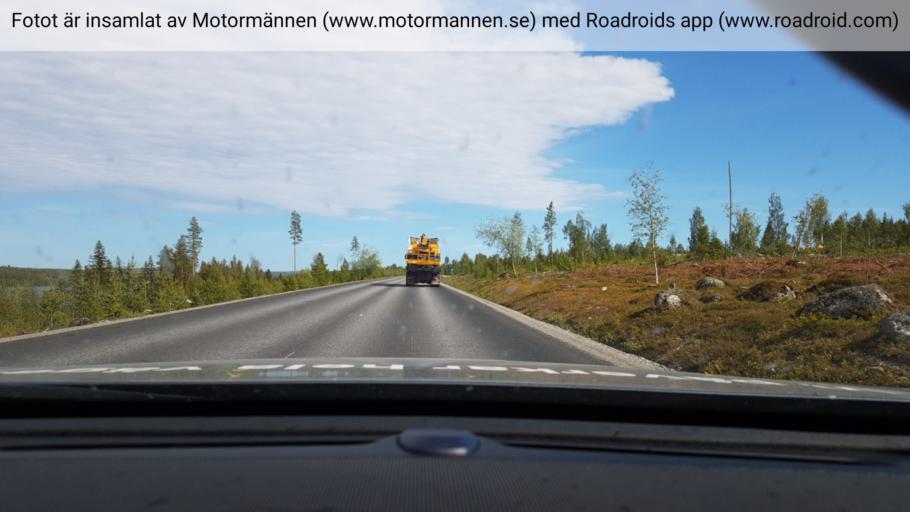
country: SE
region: Vaesterbotten
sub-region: Lycksele Kommun
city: Soderfors
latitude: 64.8375
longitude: 17.9907
